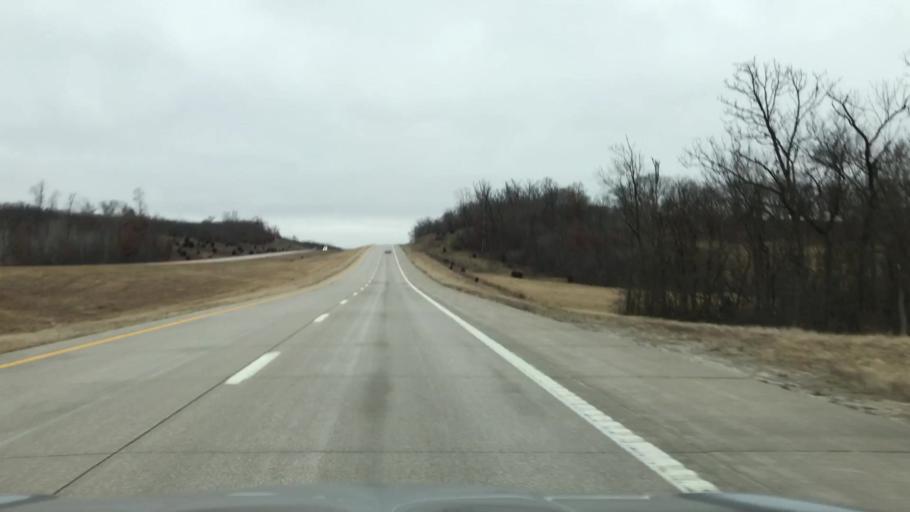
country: US
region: Missouri
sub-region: Linn County
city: Marceline
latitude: 39.7584
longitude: -92.8538
